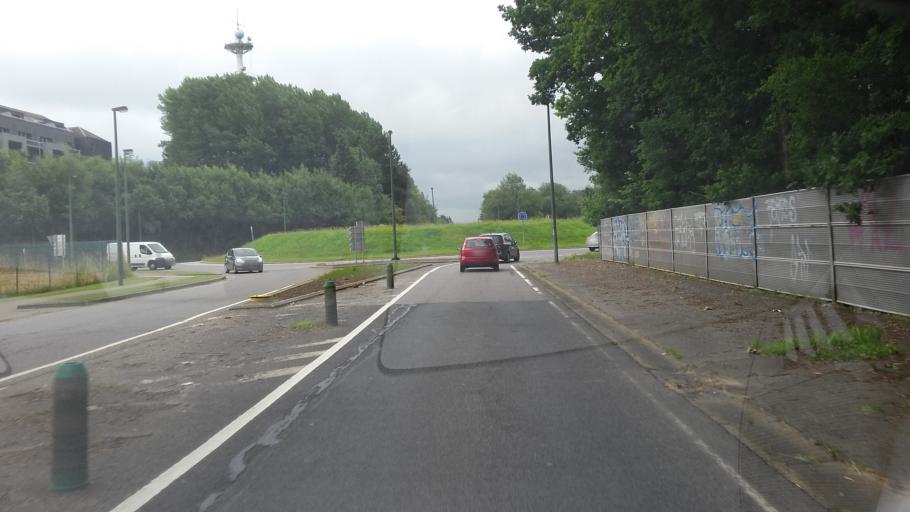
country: BE
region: Wallonia
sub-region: Province du Luxembourg
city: Arlon
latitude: 49.6892
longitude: 5.8183
